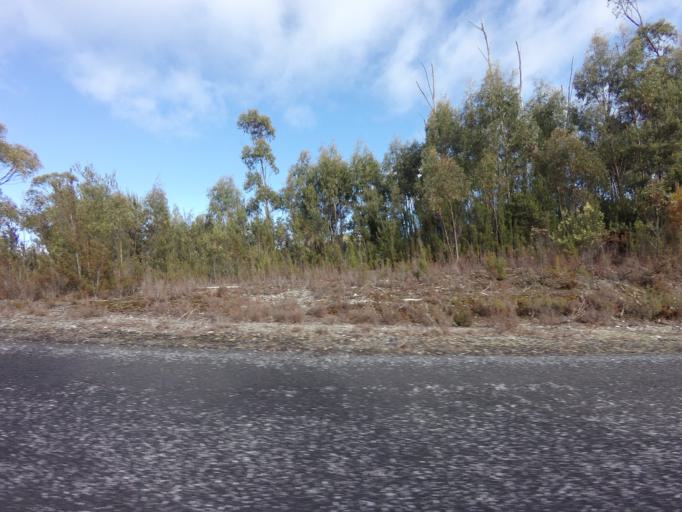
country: AU
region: Tasmania
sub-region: Huon Valley
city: Geeveston
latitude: -42.8099
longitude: 146.0967
